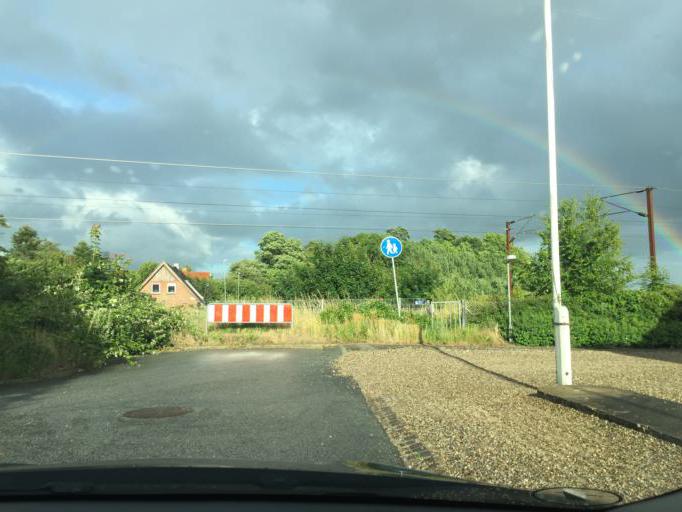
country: DK
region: South Denmark
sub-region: Kolding Kommune
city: Vamdrup
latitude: 55.3845
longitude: 9.2699
